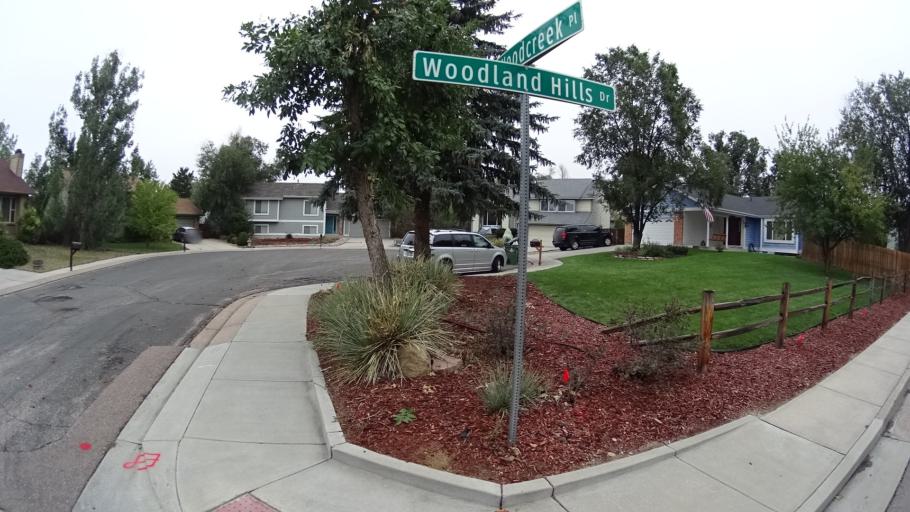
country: US
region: Colorado
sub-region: El Paso County
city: Cimarron Hills
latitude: 38.9310
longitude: -104.7706
